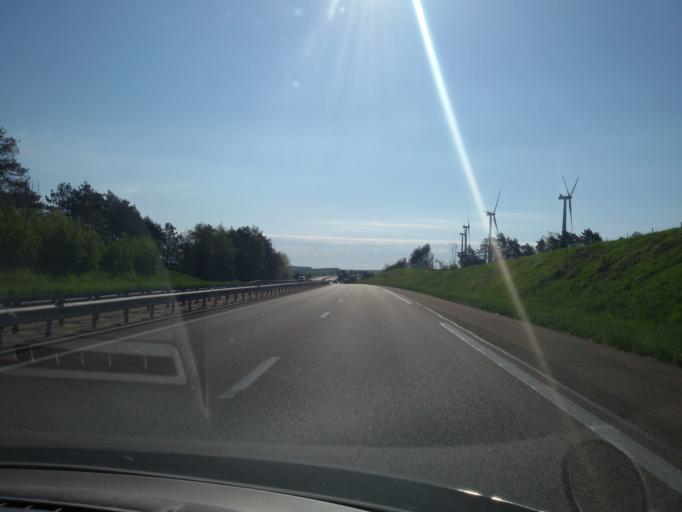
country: FR
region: Bourgogne
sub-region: Departement de l'Yonne
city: Saint-Bris-le-Vineux
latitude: 47.7775
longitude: 3.6949
